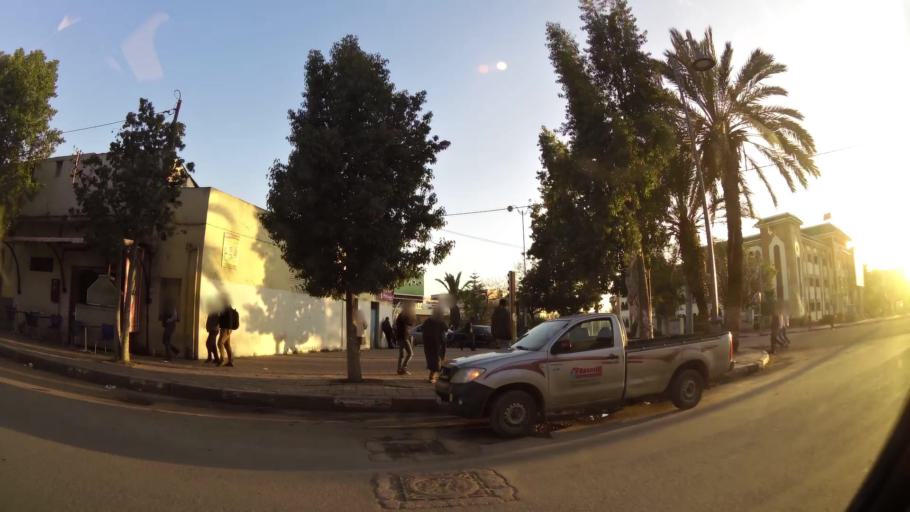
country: MA
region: Chaouia-Ouardigha
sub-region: Settat Province
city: Settat
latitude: 33.0005
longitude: -7.6184
